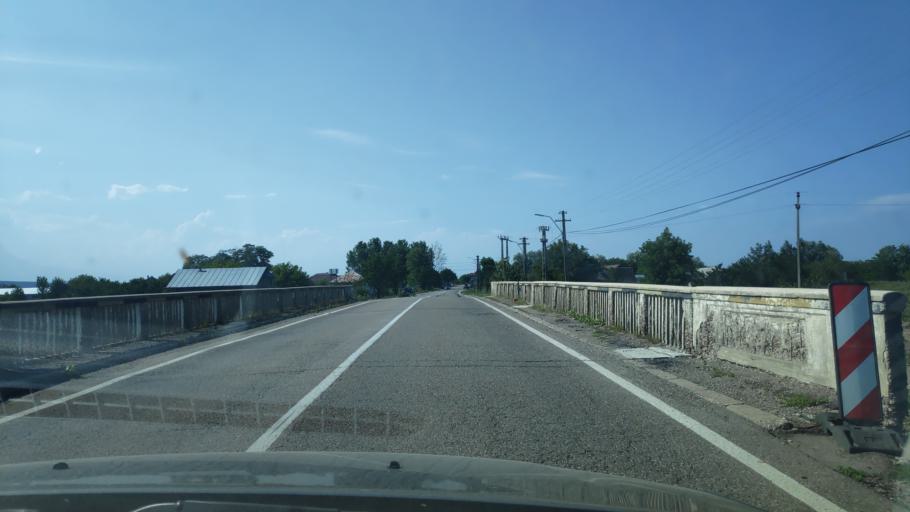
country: RO
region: Suceava
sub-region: Comuna Boroaia
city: Boroaia
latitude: 47.3789
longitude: 26.3193
